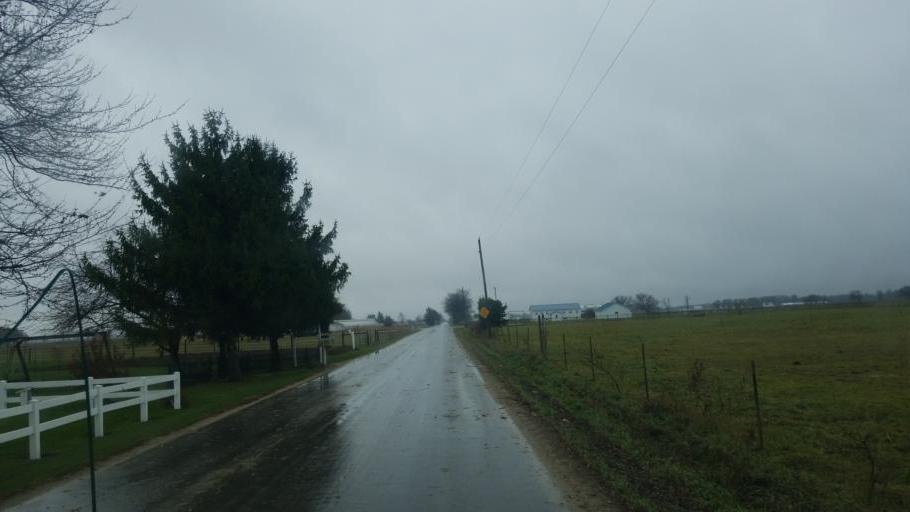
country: US
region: Indiana
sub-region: Adams County
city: Berne
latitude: 40.7188
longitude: -84.9174
